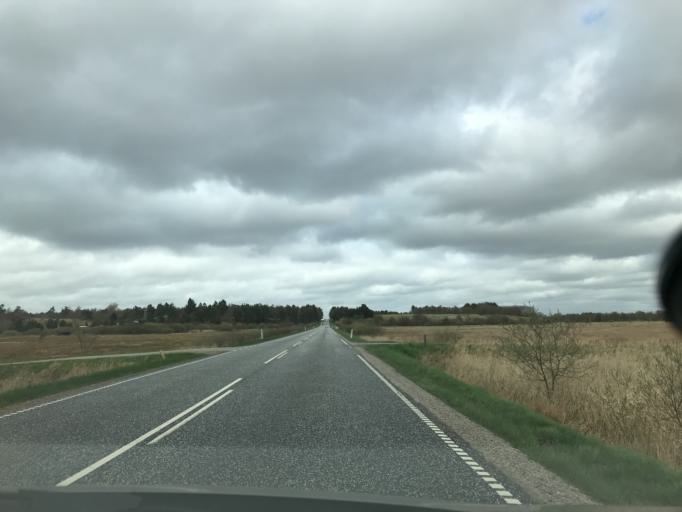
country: DK
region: Central Jutland
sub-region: Skive Kommune
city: Skive
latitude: 56.5177
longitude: 8.9559
